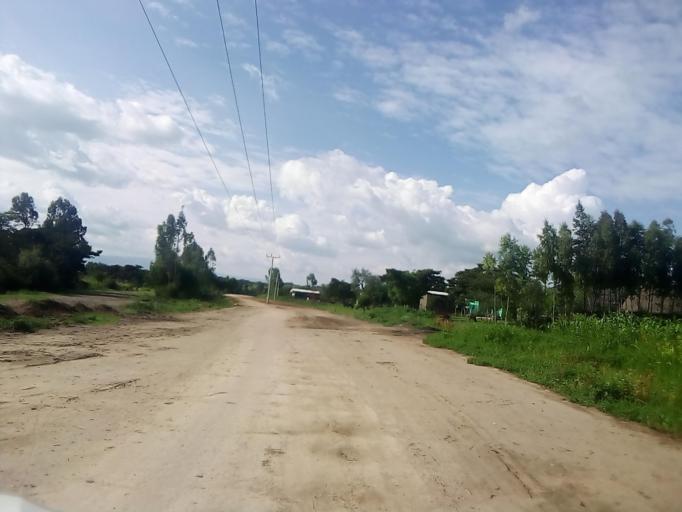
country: ET
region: Southern Nations, Nationalities, and People's Region
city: K'olito
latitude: 7.6140
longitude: 38.0650
